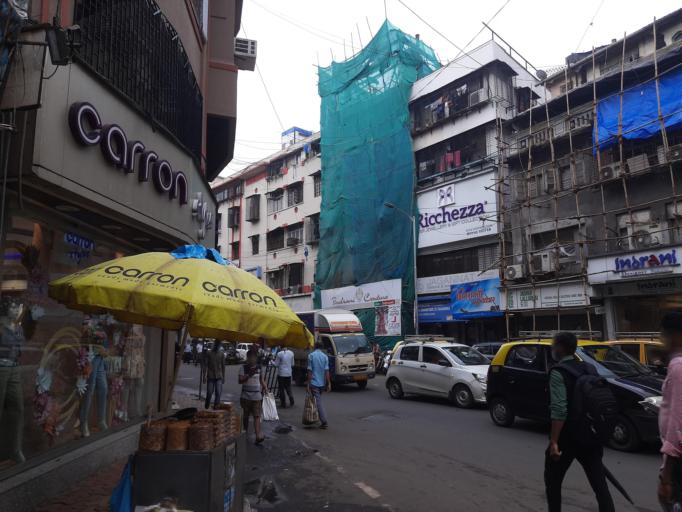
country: IN
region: Maharashtra
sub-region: Raigarh
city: Uran
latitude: 18.9509
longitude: 72.8289
